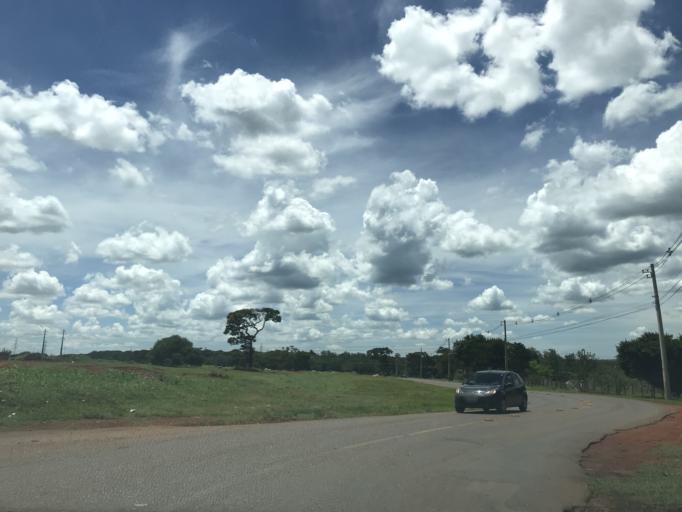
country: BR
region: Federal District
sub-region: Brasilia
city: Brasilia
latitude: -15.7329
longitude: -47.9083
